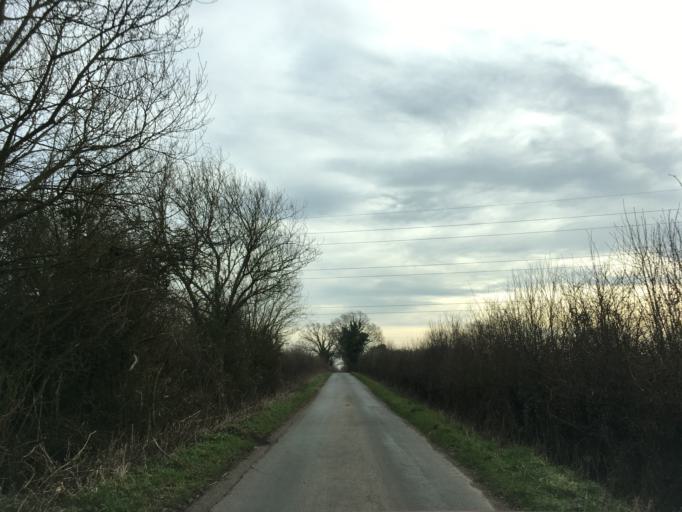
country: GB
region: England
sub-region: South Gloucestershire
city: Yate
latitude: 51.5688
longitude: -2.4251
